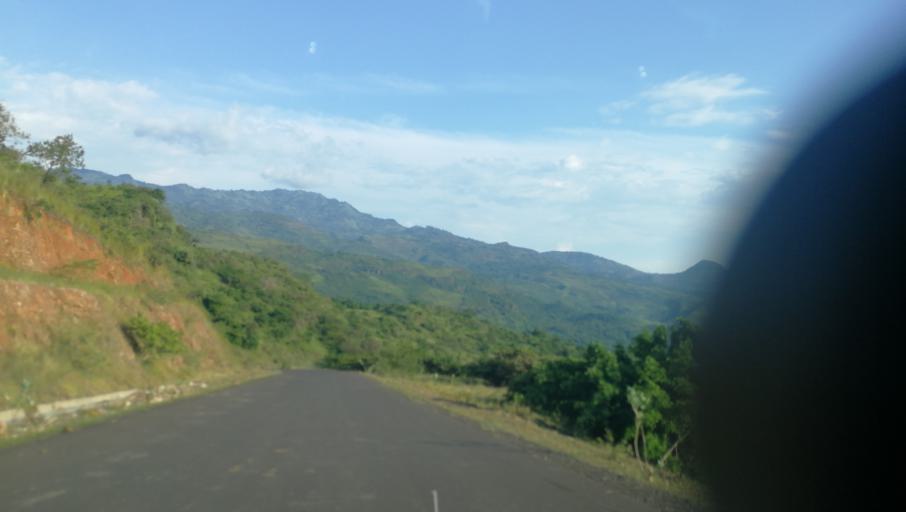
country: ET
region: Southern Nations, Nationalities, and People's Region
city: Areka
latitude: 6.8302
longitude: 37.3082
